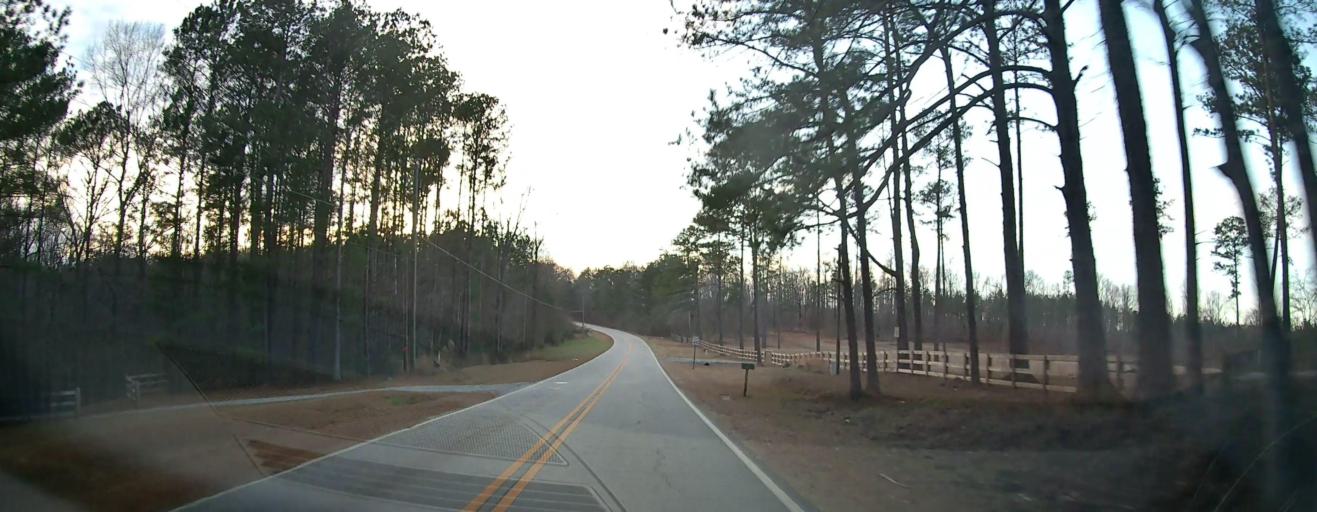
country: US
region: Georgia
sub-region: Harris County
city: Hamilton
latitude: 32.6000
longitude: -84.8881
